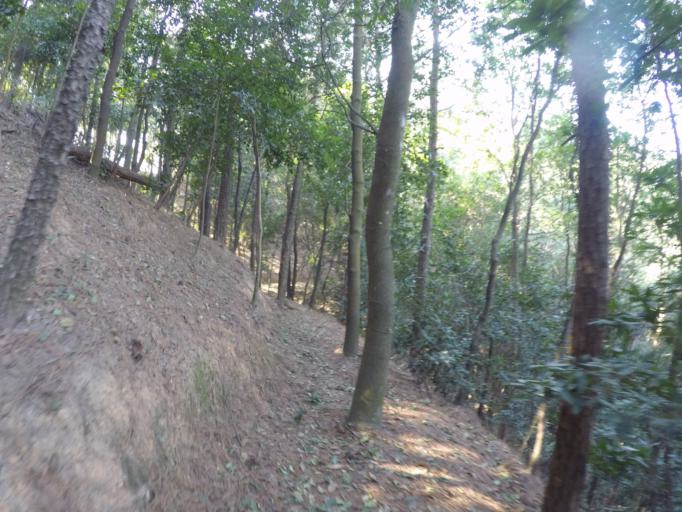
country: CN
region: Guangdong
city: Huancheng
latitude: 22.4687
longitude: 113.4125
